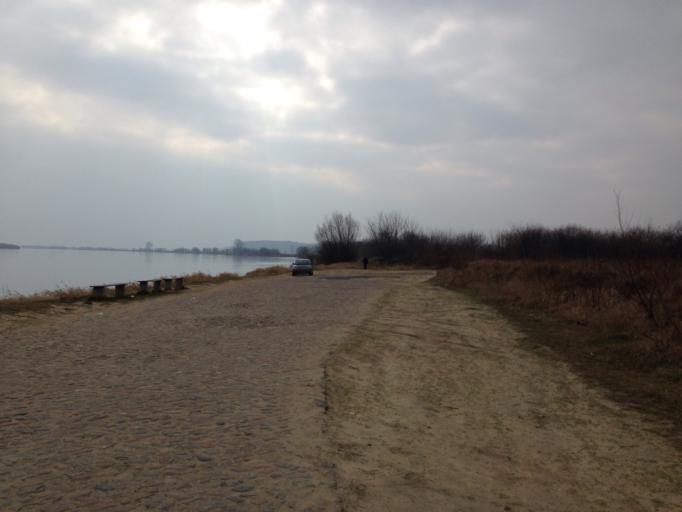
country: PL
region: Pomeranian Voivodeship
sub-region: Powiat tczewski
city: Gniew
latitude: 53.8338
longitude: 18.8368
